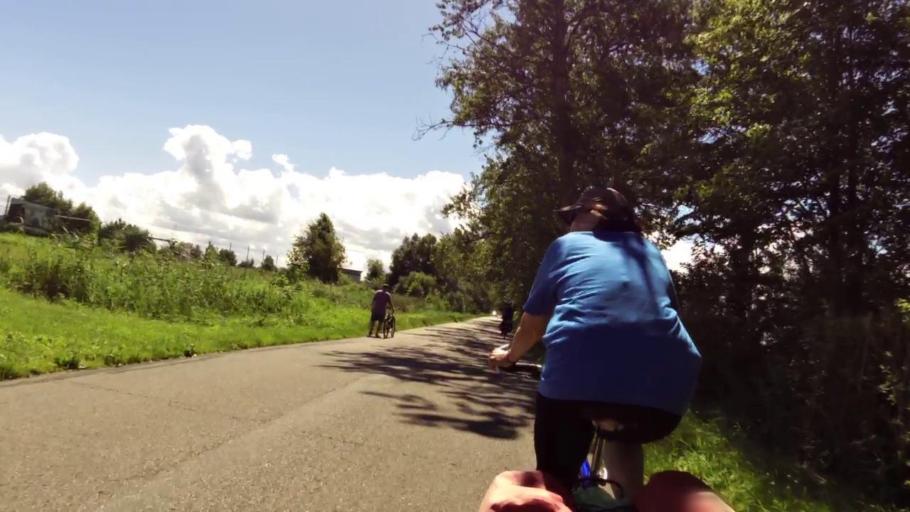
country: PL
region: West Pomeranian Voivodeship
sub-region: Powiat koszalinski
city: Sianow
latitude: 54.2906
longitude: 16.2104
